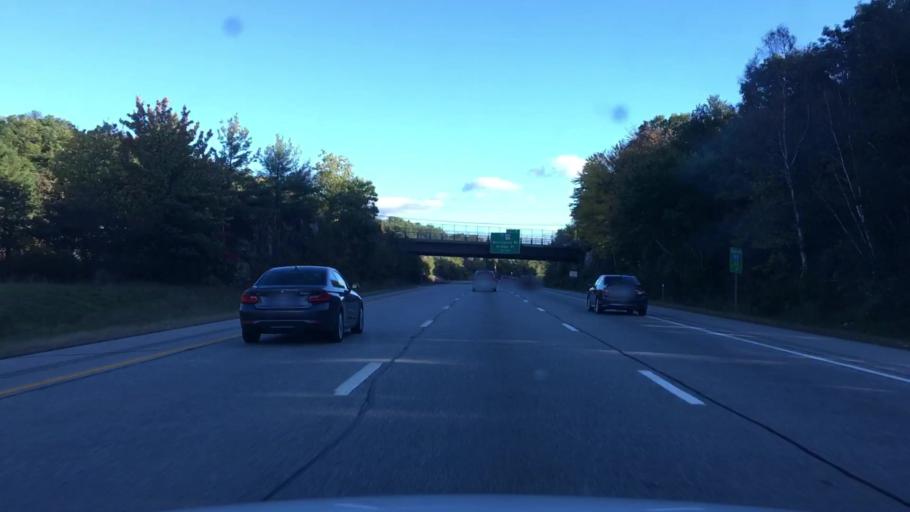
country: US
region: New Hampshire
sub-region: Merrimack County
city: South Hooksett
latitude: 43.0146
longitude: -71.4374
